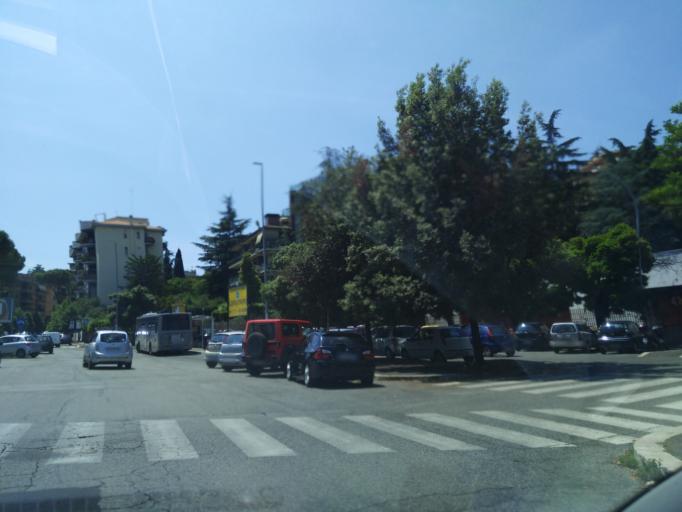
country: IT
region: Latium
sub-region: Citta metropolitana di Roma Capitale
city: Vitinia
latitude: 41.8084
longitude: 12.4442
